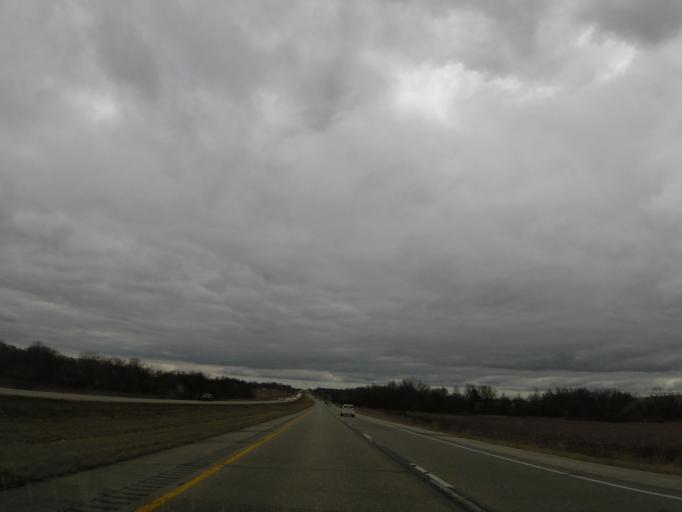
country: US
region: Iowa
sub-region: Linn County
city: Center Point
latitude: 42.1499
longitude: -91.7485
